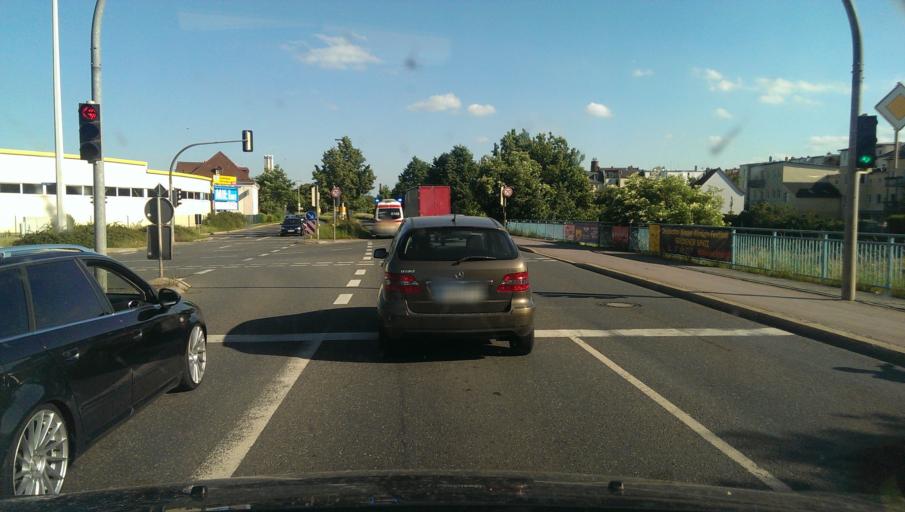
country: DE
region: Thuringia
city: Gera
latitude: 50.8698
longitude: 12.0751
